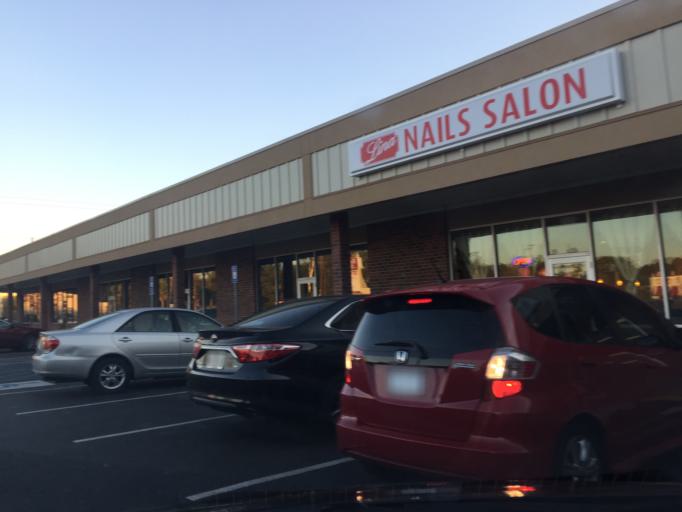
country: US
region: Georgia
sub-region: Chatham County
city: Savannah
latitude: 32.0267
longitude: -81.1097
